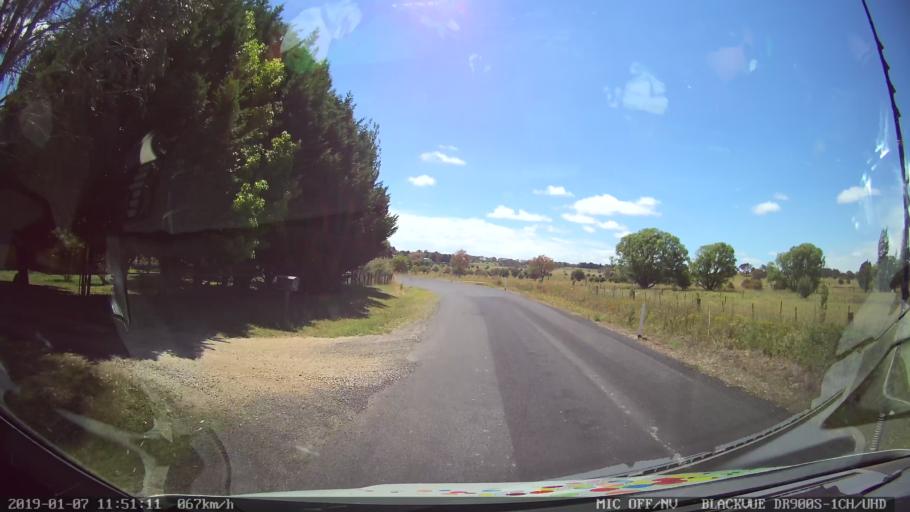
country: AU
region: New South Wales
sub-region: Guyra
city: Guyra
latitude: -30.3093
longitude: 151.6439
